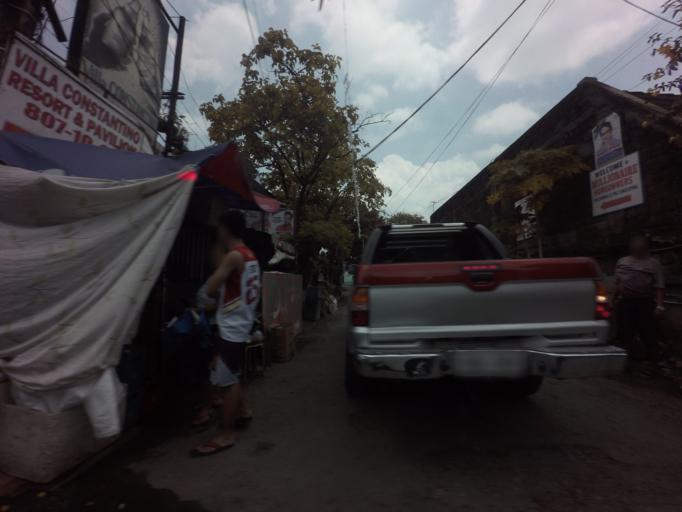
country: PH
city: Sambayanihan People's Village
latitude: 14.4334
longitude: 121.0501
